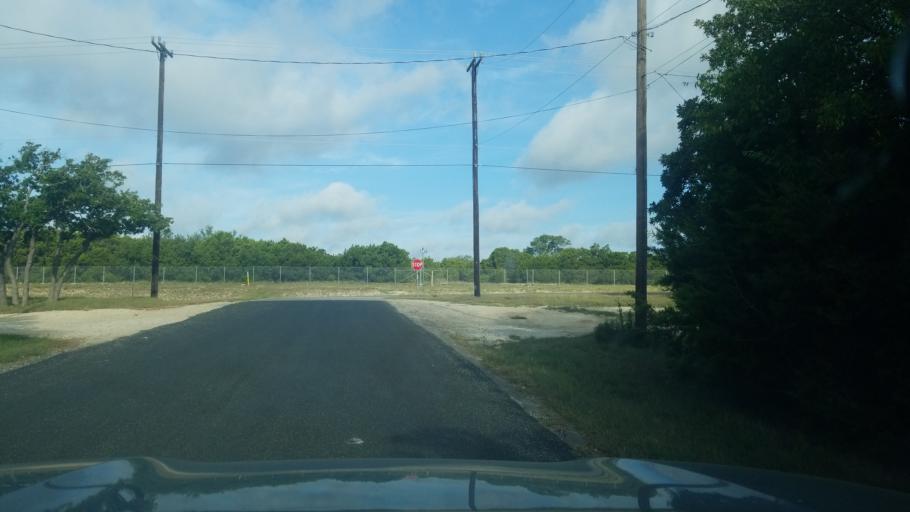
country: US
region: Texas
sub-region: Bexar County
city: Timberwood Park
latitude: 29.6956
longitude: -98.5209
